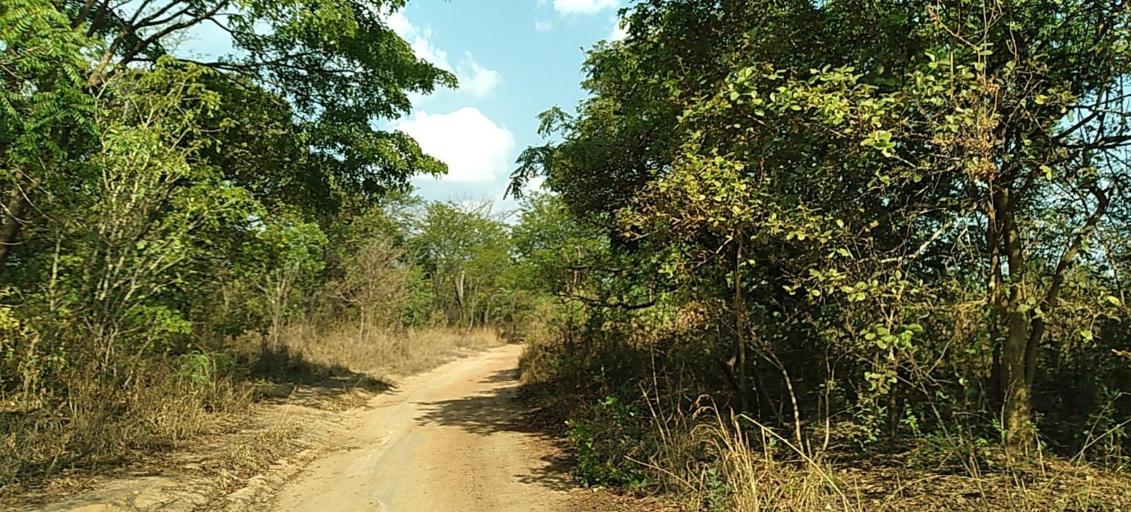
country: ZM
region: Copperbelt
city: Luanshya
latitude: -13.1539
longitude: 28.3194
